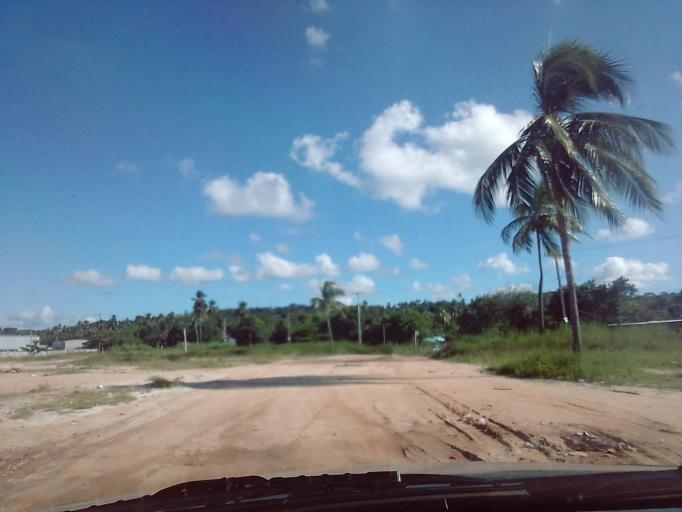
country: BR
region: Pernambuco
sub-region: Igarassu
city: Igarassu
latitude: -7.8382
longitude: -34.8457
